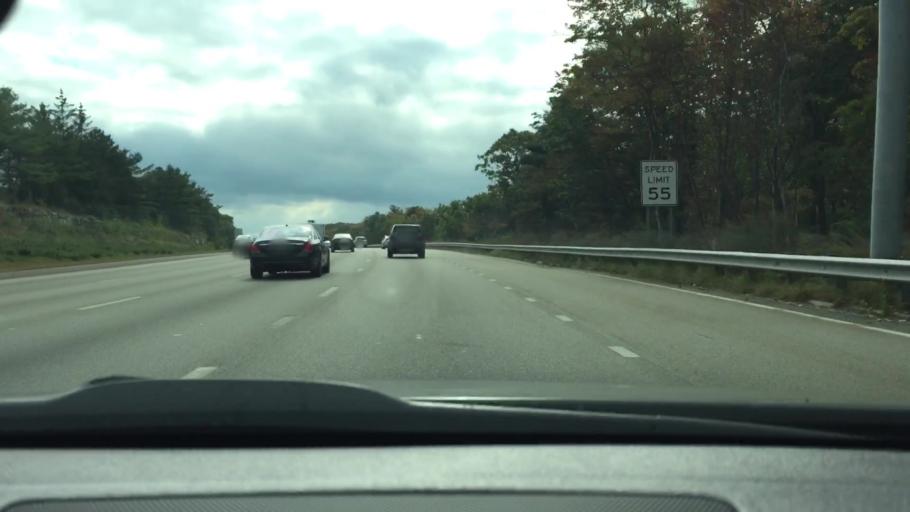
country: US
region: Massachusetts
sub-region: Norfolk County
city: Needham
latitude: 42.2614
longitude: -71.2097
